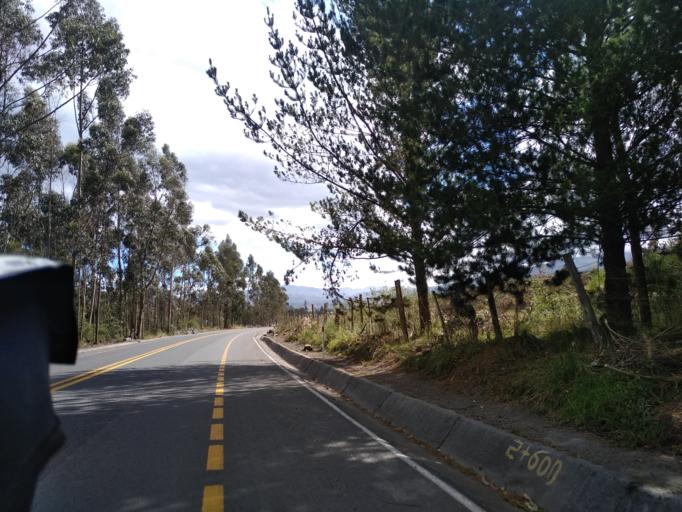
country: EC
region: Cotopaxi
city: Saquisili
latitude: -0.6980
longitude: -78.5729
